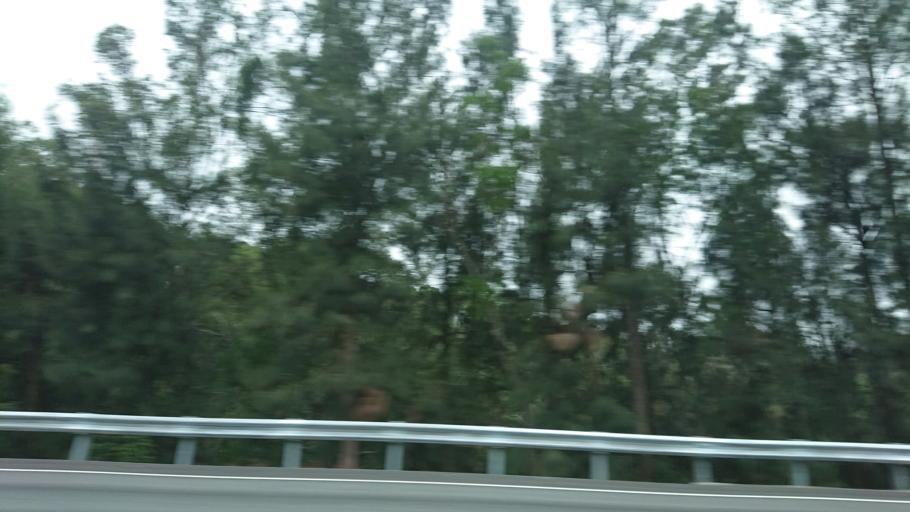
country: TW
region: Taiwan
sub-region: Hsinchu
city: Hsinchu
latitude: 24.7472
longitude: 120.9263
